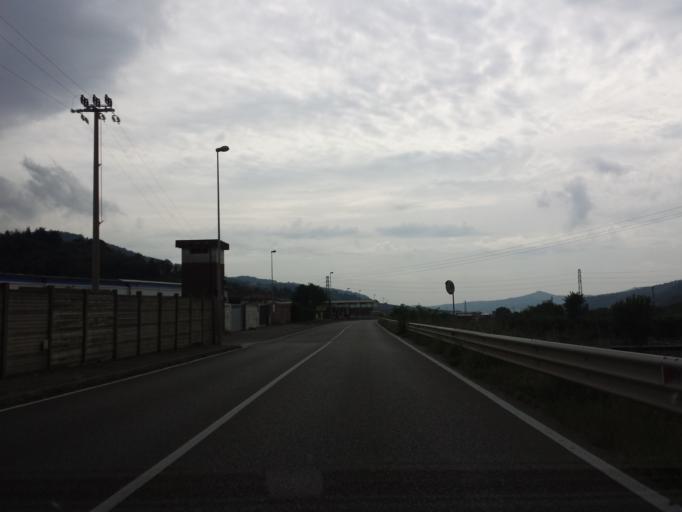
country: IT
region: Veneto
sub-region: Provincia di Verona
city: San Giovanni Ilarione
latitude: 45.5161
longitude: 11.2372
